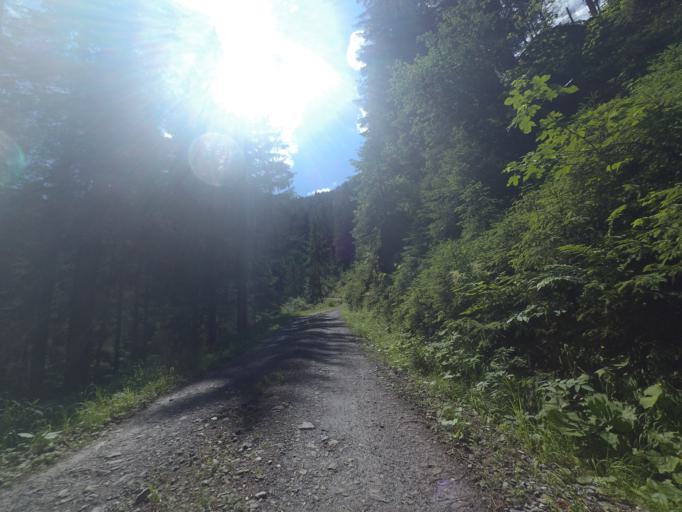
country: AT
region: Salzburg
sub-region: Politischer Bezirk Sankt Johann im Pongau
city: Schwarzach im Pongau
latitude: 47.3051
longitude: 13.1495
